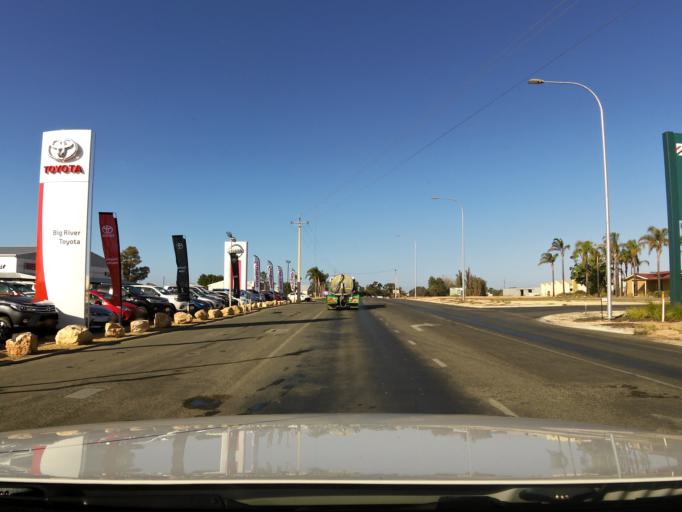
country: AU
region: South Australia
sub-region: Berri and Barmera
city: Berri
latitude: -34.2606
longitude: 140.6144
